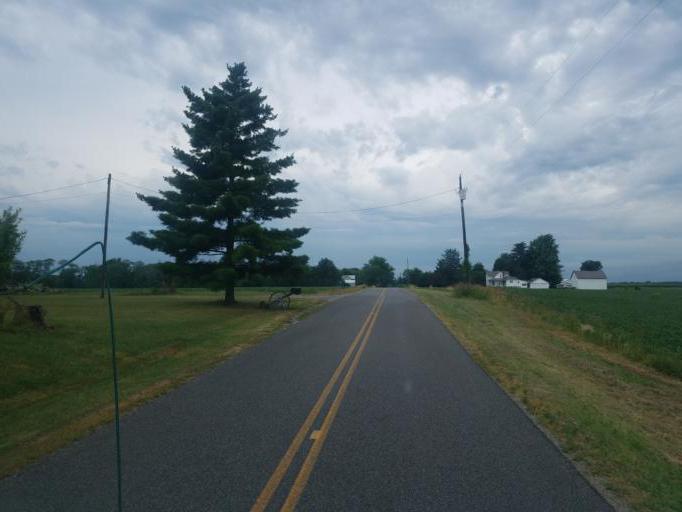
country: US
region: Ohio
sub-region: Paulding County
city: Antwerp
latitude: 41.2375
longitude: -84.7095
